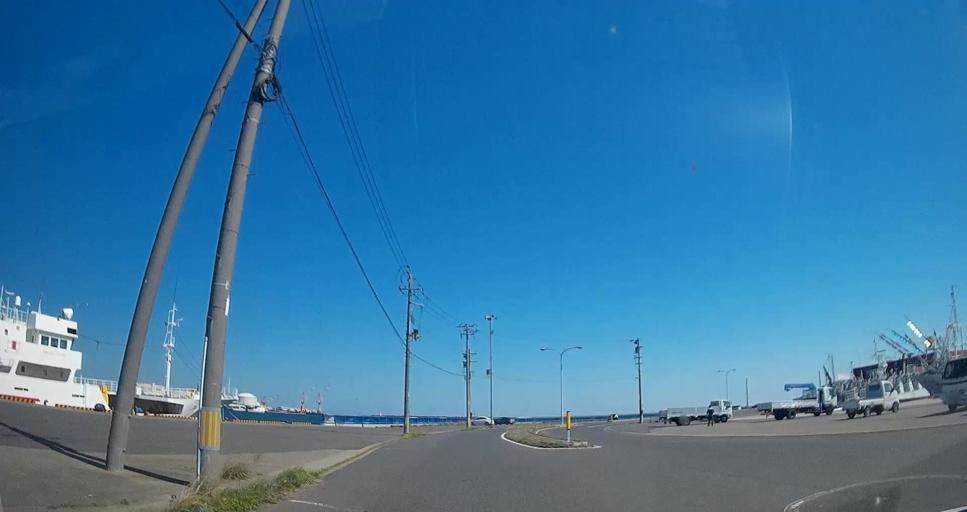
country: JP
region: Aomori
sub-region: Hachinohe Shi
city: Uchimaru
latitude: 40.5300
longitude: 141.5359
